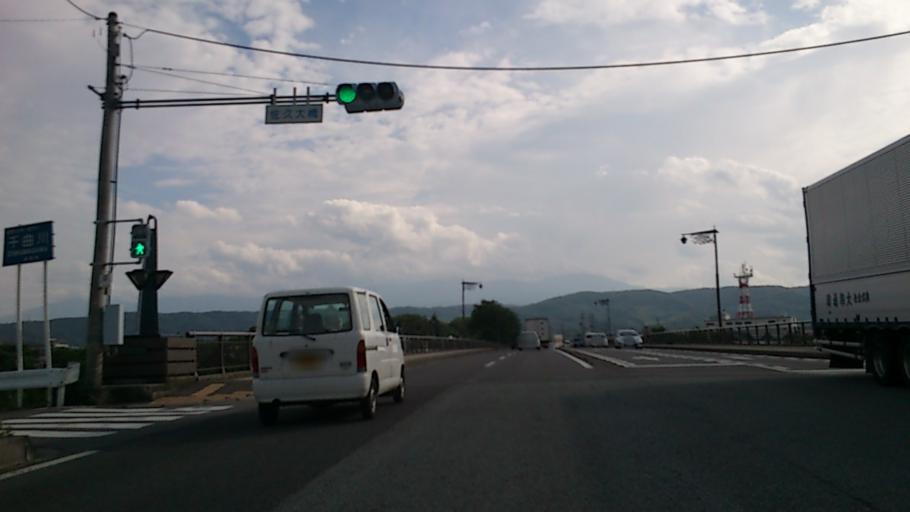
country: JP
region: Nagano
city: Saku
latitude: 36.2301
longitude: 138.4736
